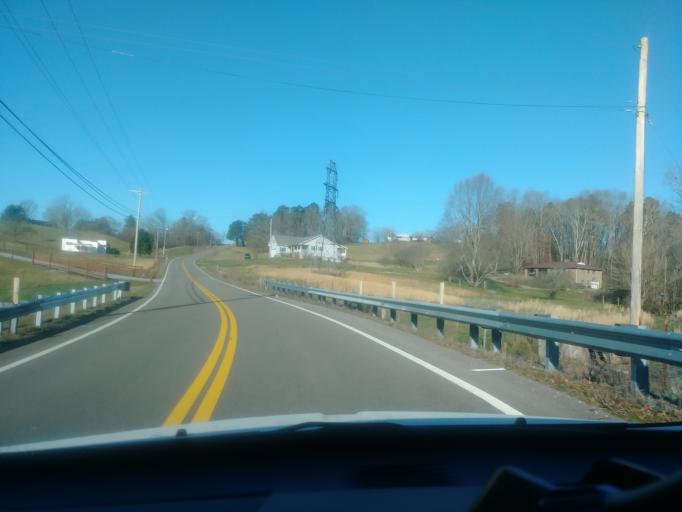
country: US
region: Tennessee
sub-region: Greene County
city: Mosheim
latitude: 36.1148
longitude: -82.9520
